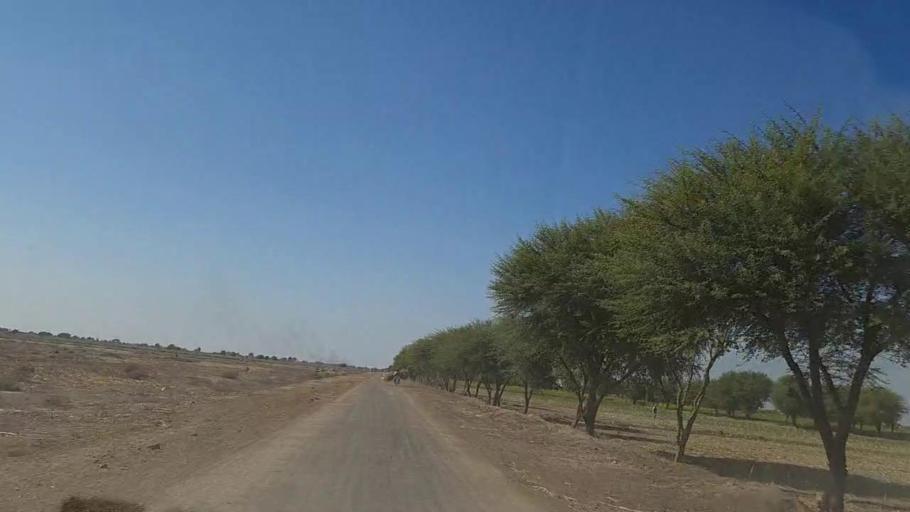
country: PK
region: Sindh
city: Digri
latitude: 25.1168
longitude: 69.0465
